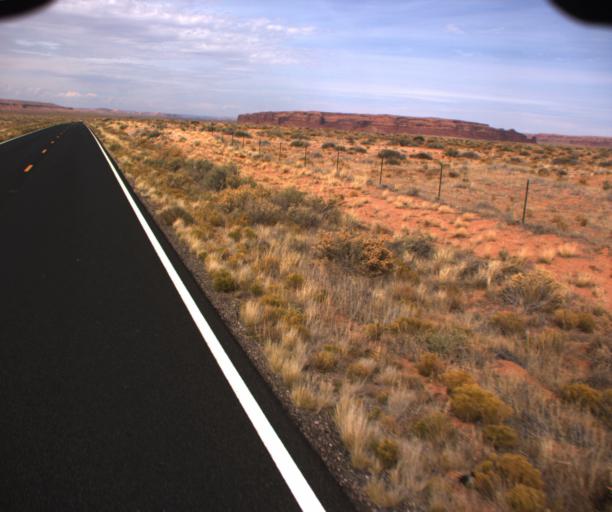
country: US
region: Arizona
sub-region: Apache County
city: Many Farms
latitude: 36.5594
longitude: -109.5386
